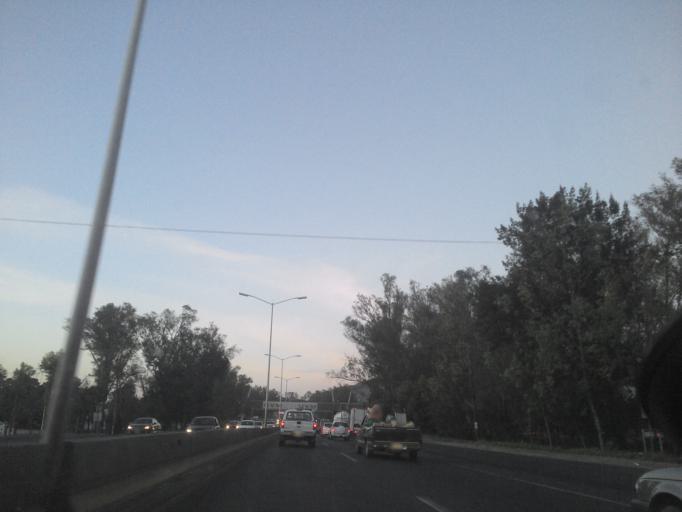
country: MX
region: Jalisco
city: Guadalajara
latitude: 20.6803
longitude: -103.4553
